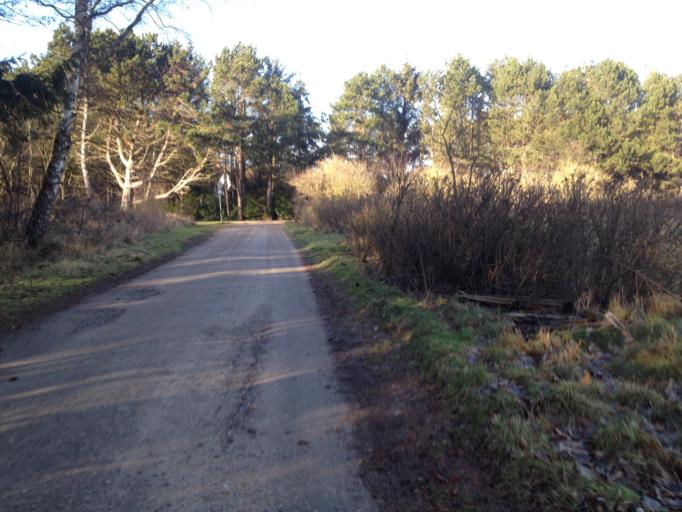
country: DE
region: Schleswig-Holstein
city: Nebel
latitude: 54.6456
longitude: 8.3470
